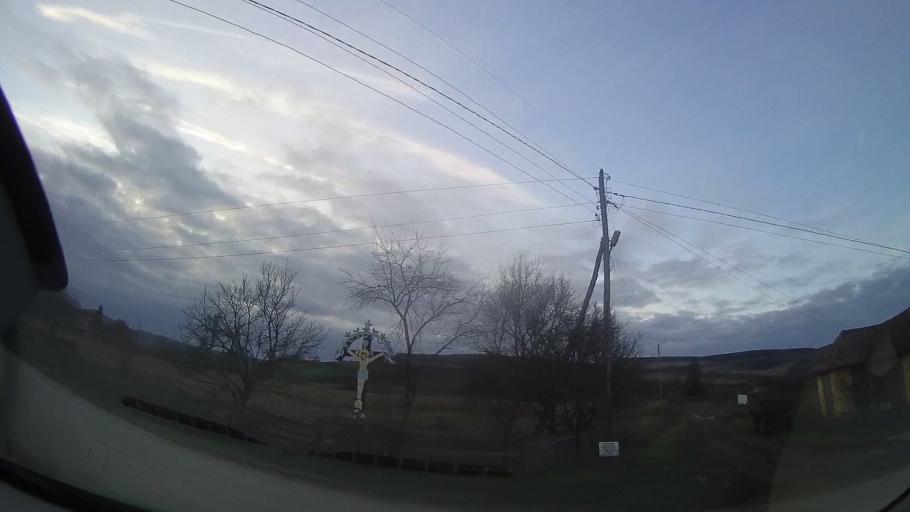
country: RO
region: Cluj
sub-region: Comuna Palatca
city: Palatca
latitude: 46.8690
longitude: 24.0130
